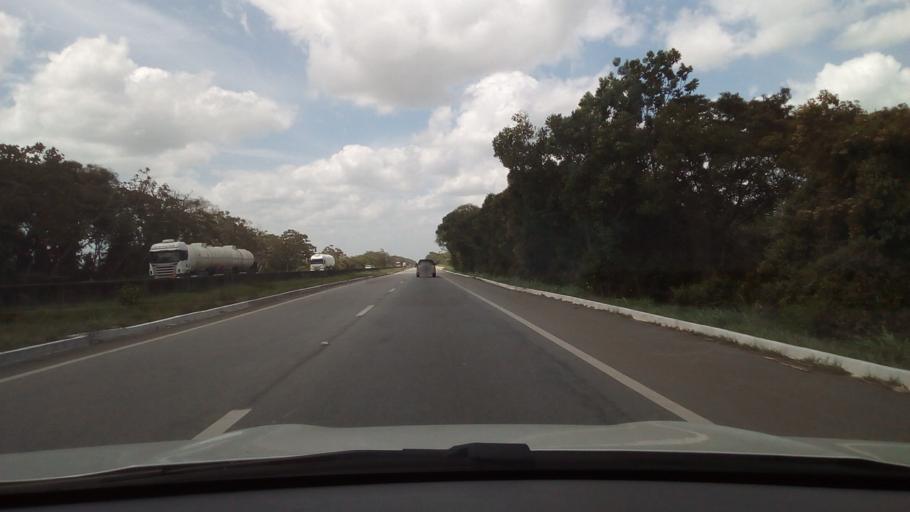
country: BR
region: Paraiba
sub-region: Mamanguape
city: Mamanguape
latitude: -6.9076
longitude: -35.1166
